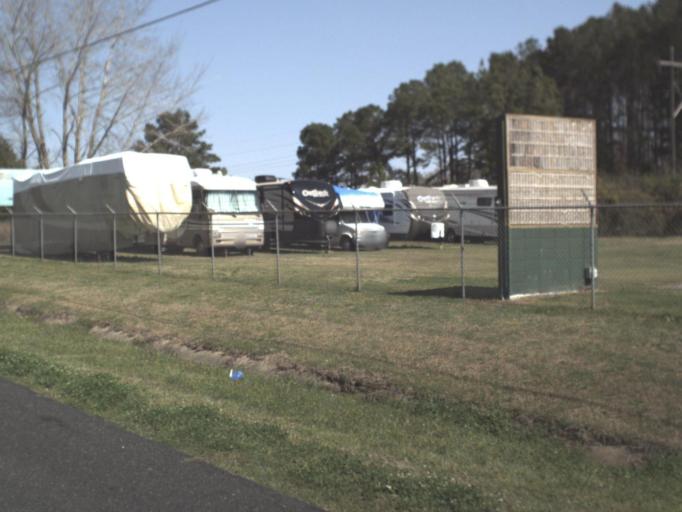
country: US
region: Florida
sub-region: Gadsden County
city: Havana
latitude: 30.5852
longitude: -84.4020
